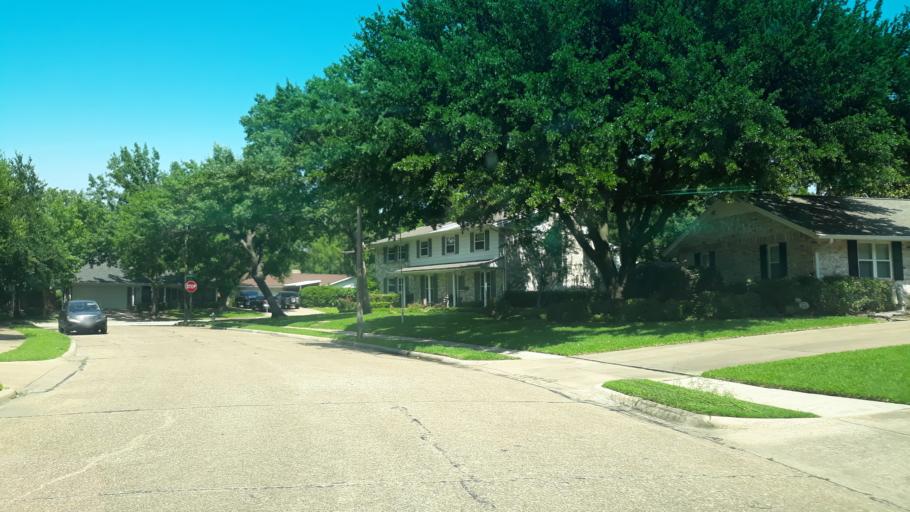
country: US
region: Texas
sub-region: Dallas County
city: Irving
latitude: 32.8573
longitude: -96.9581
